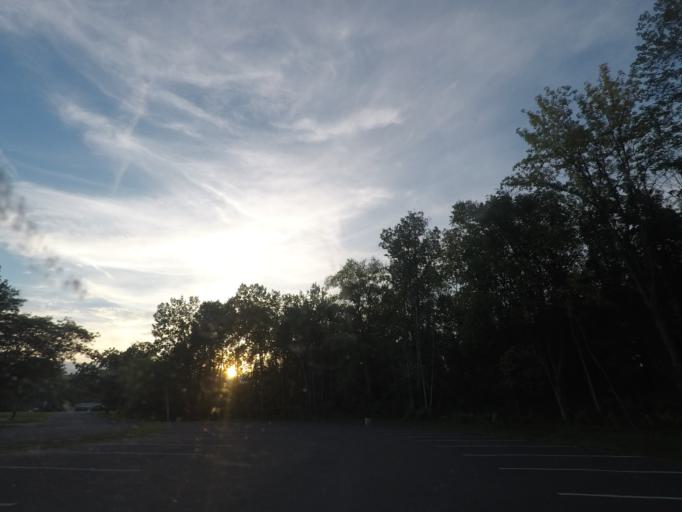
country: US
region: New York
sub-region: Schenectady County
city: Niskayuna
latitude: 42.7647
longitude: -73.8133
